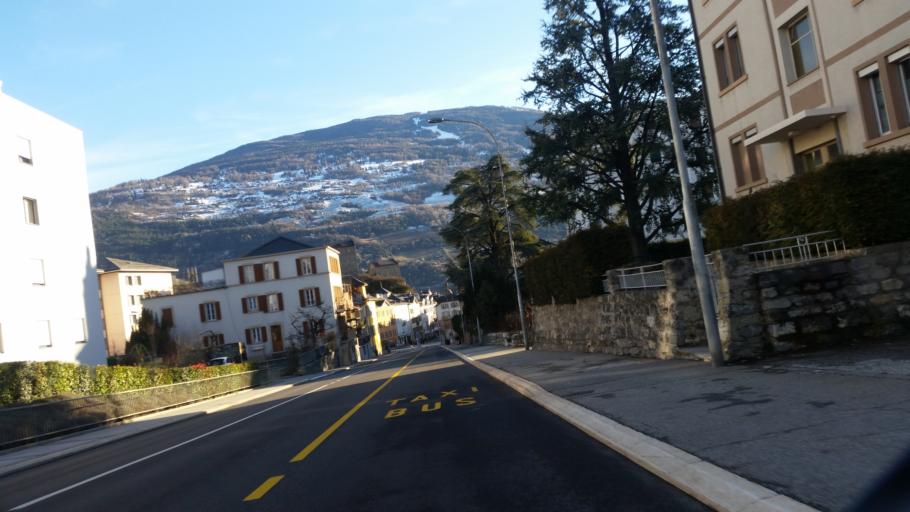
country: CH
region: Valais
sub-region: Sion District
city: Sitten
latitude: 46.2374
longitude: 7.3602
